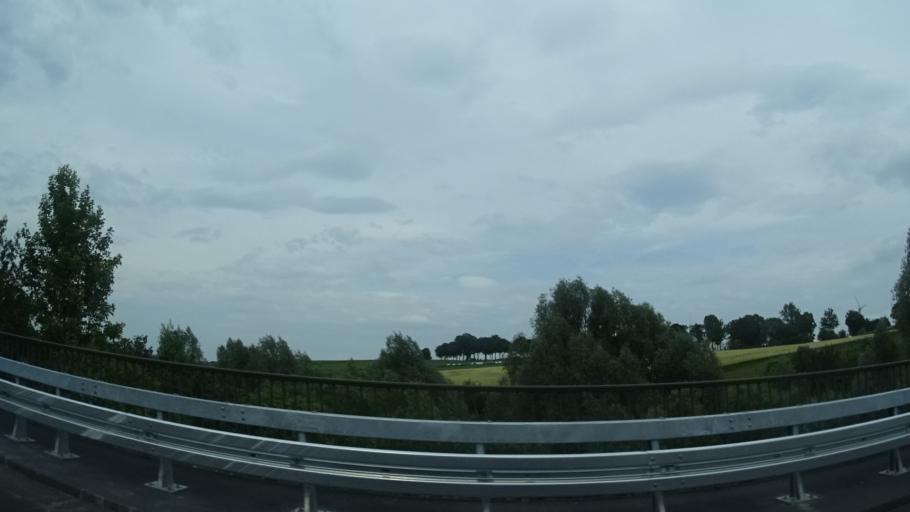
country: DE
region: North Rhine-Westphalia
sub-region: Regierungsbezirk Detmold
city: Willebadessen
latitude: 51.6000
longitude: 9.1396
